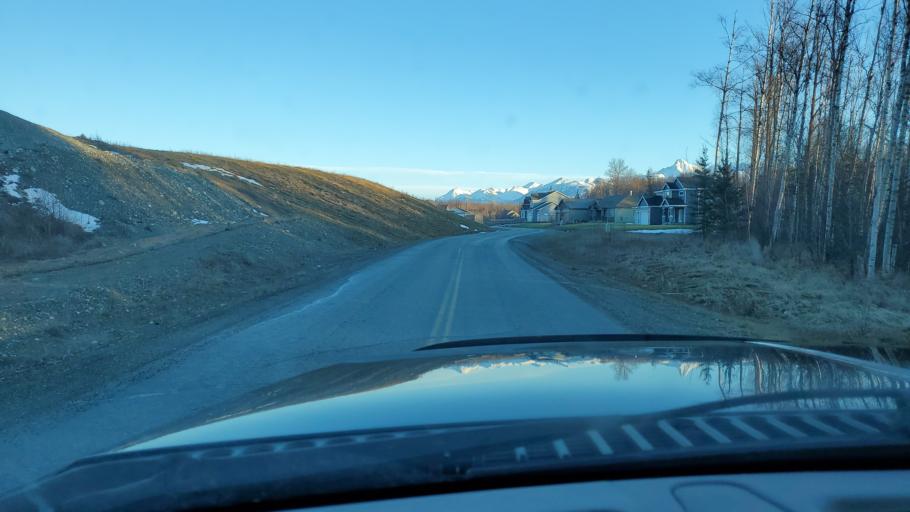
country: US
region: Alaska
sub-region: Matanuska-Susitna Borough
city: Gateway
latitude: 61.5860
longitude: -149.2626
